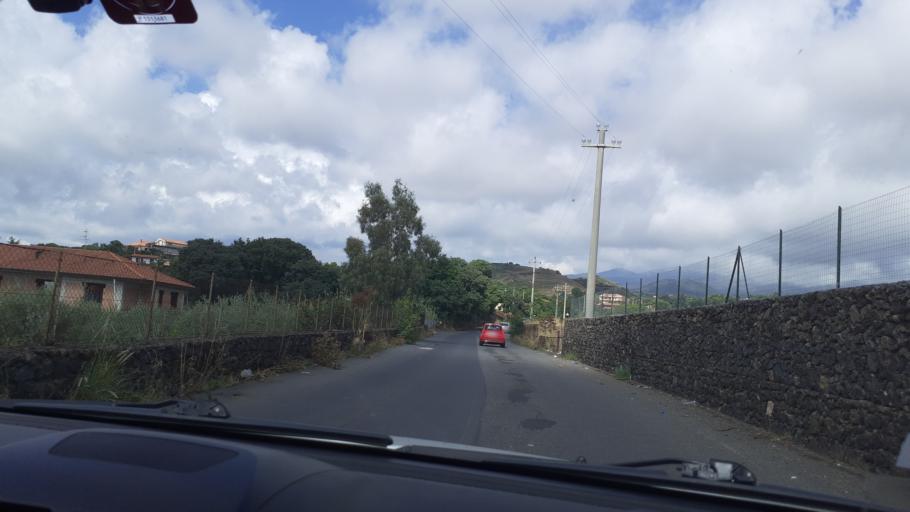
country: IT
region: Sicily
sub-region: Catania
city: Trecastagni
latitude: 37.6033
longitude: 15.0723
